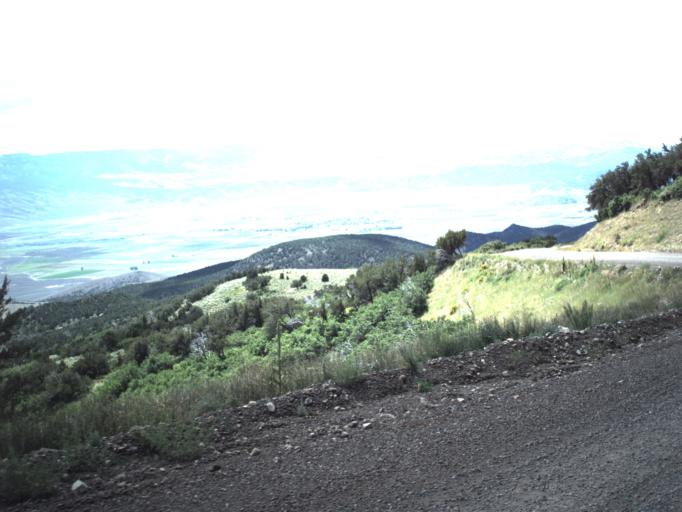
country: US
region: Utah
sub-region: Piute County
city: Junction
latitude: 38.2584
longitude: -112.3188
